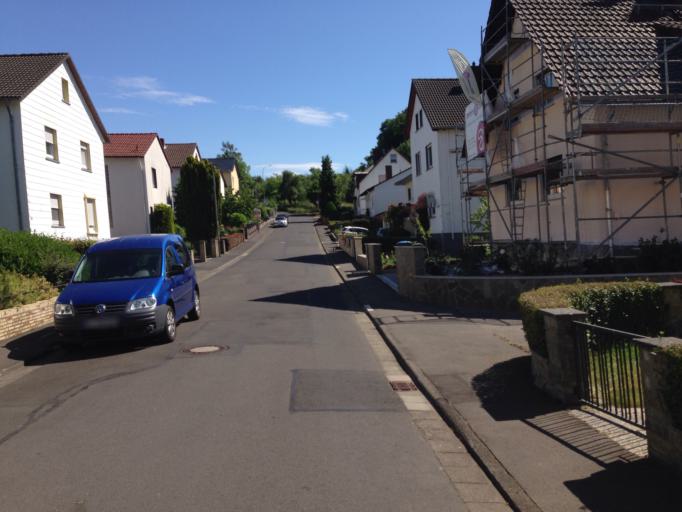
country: DE
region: Hesse
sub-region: Regierungsbezirk Giessen
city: Alten Buseck
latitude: 50.6007
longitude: 8.7453
